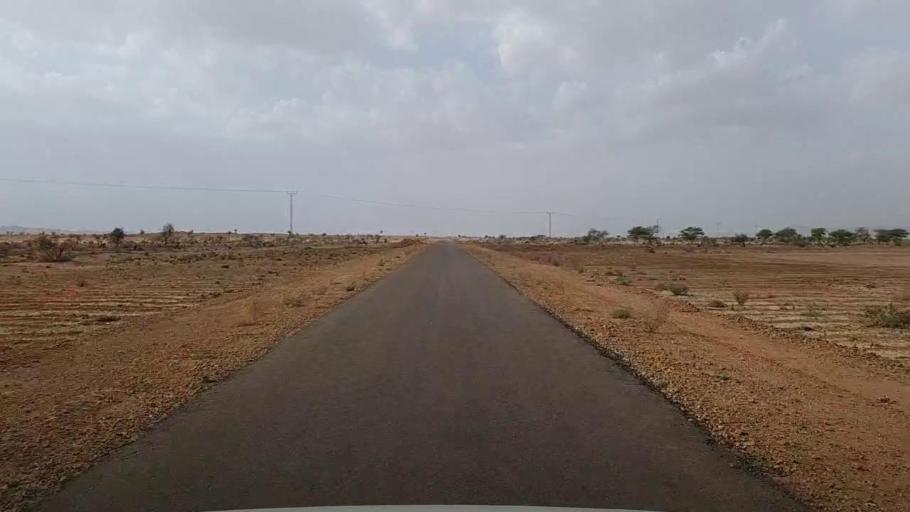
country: PK
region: Sindh
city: Jamshoro
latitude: 25.4611
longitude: 67.6774
